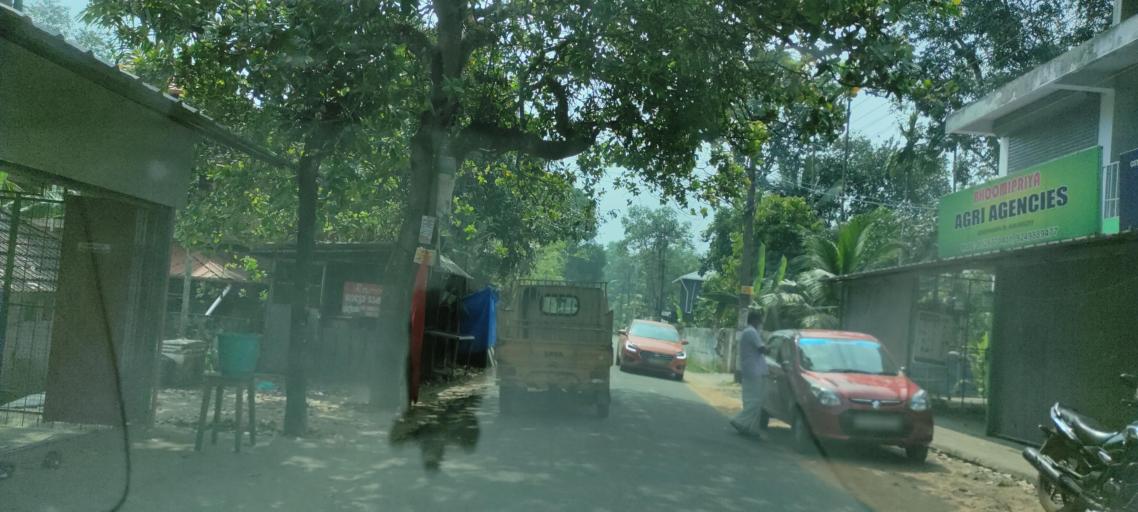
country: IN
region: Kerala
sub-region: Alappuzha
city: Shertallai
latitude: 9.6151
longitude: 76.3474
